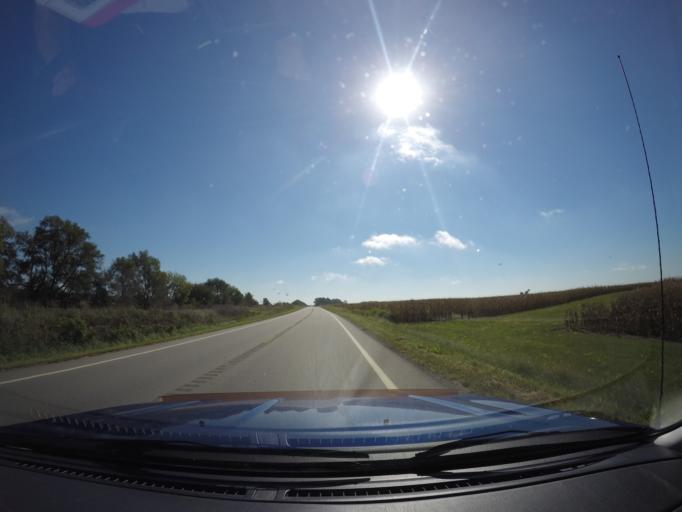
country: US
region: Kansas
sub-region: Shawnee County
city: Rossville
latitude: 39.1211
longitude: -95.9228
